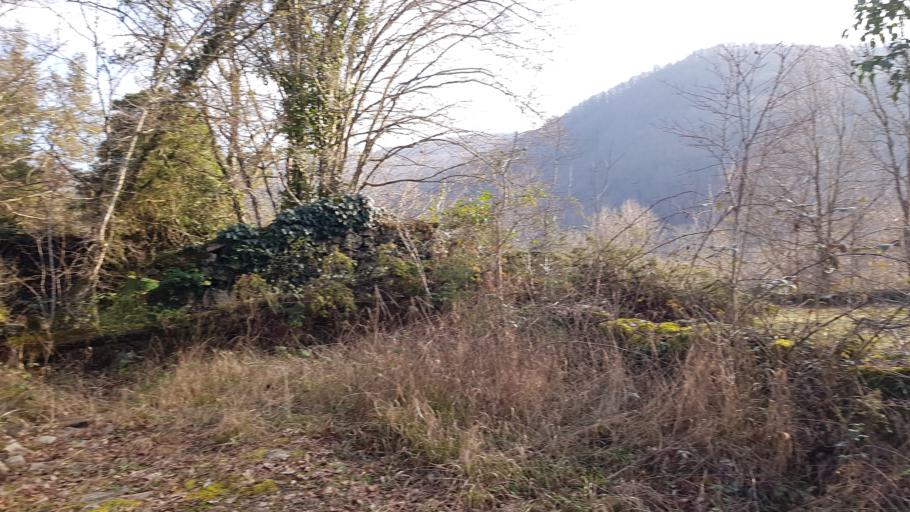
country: SI
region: Koper-Capodistria
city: Prade
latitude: 45.4692
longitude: 13.7643
